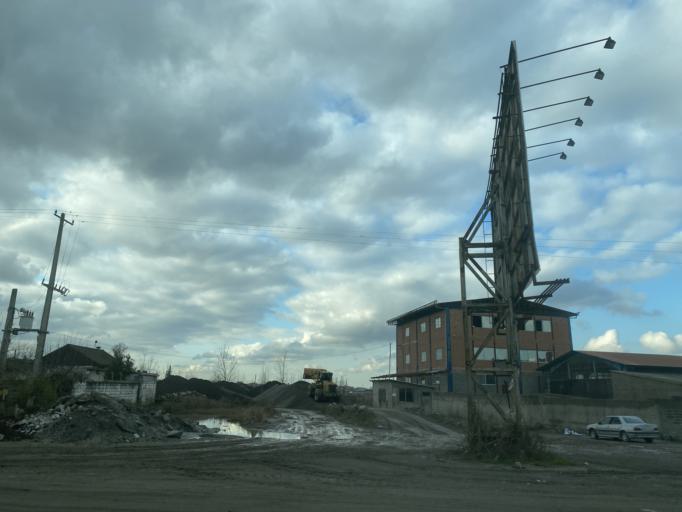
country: IR
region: Mazandaran
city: Amol
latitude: 36.4469
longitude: 52.3898
